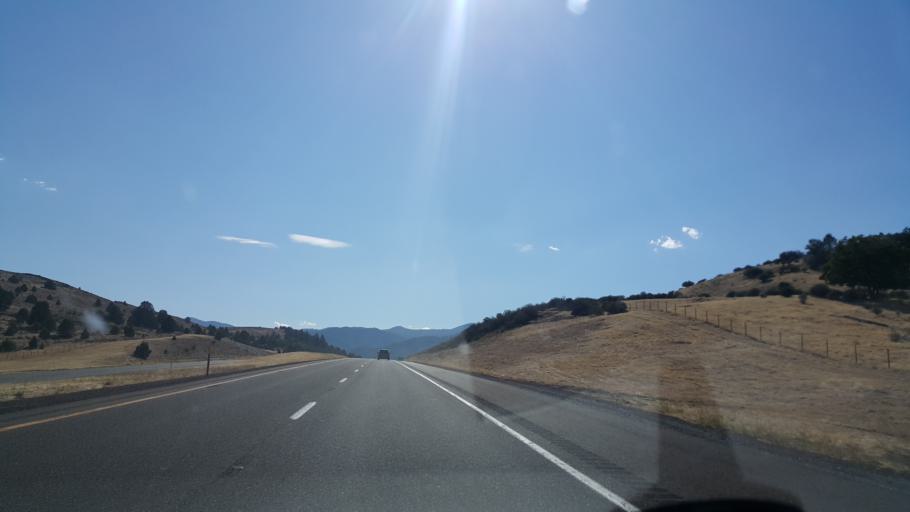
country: US
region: California
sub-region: Siskiyou County
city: Yreka
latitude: 41.7540
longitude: -122.6076
